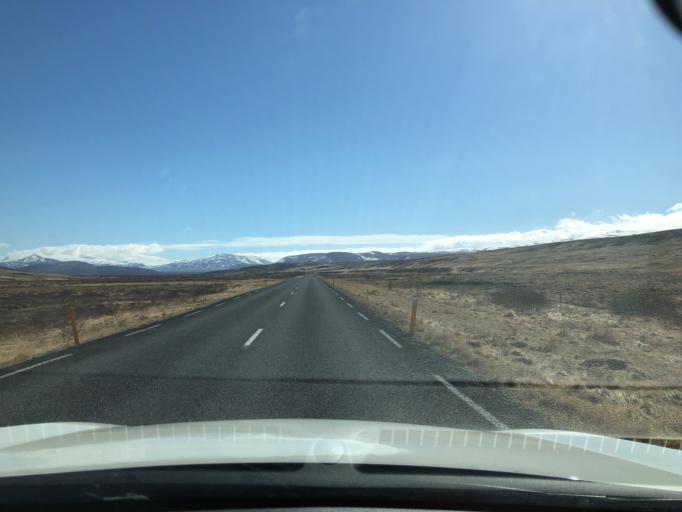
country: IS
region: South
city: Hveragerdi
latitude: 64.7016
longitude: -21.1009
